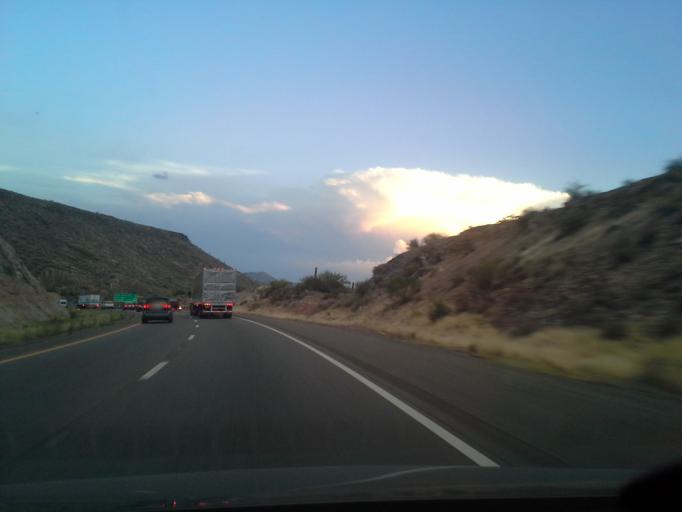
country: US
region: Arizona
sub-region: Yavapai County
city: Black Canyon City
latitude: 34.1270
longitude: -112.1506
